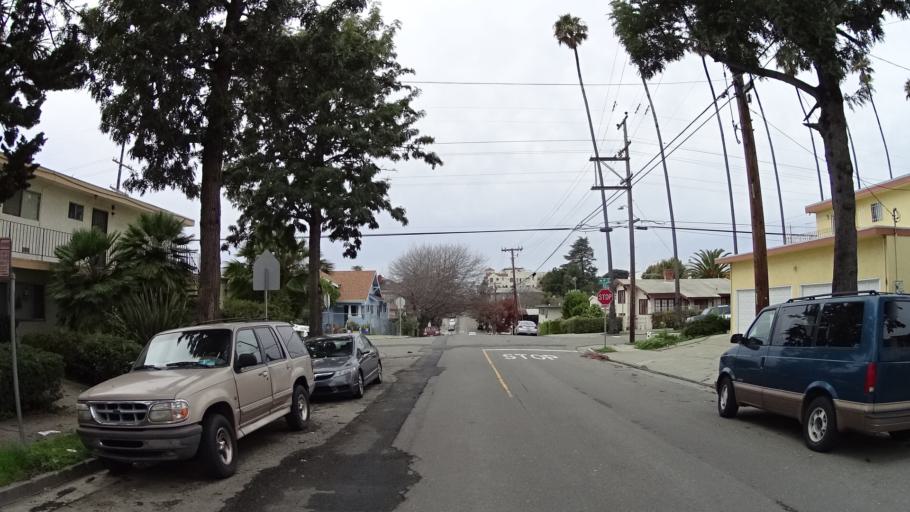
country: US
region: California
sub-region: Alameda County
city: Piedmont
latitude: 37.7991
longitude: -122.2411
